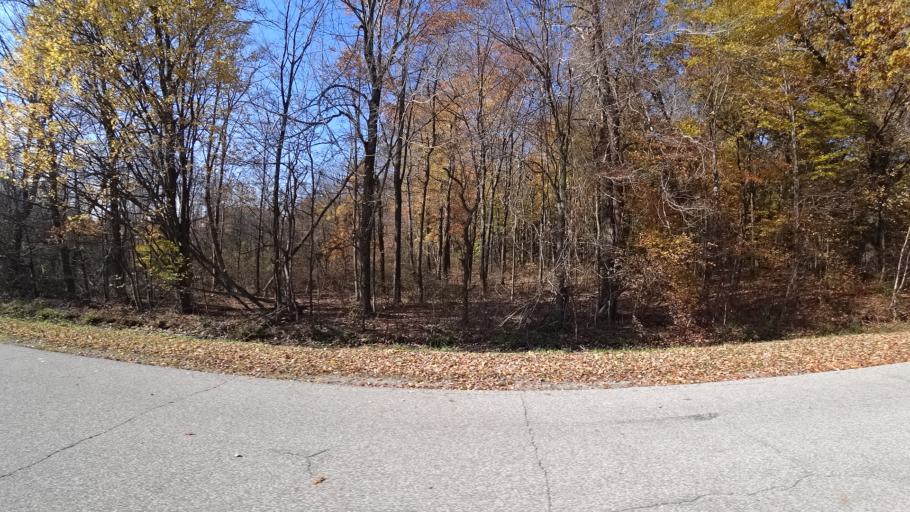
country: US
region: Indiana
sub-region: LaPorte County
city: Long Beach
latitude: 41.7355
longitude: -86.8310
